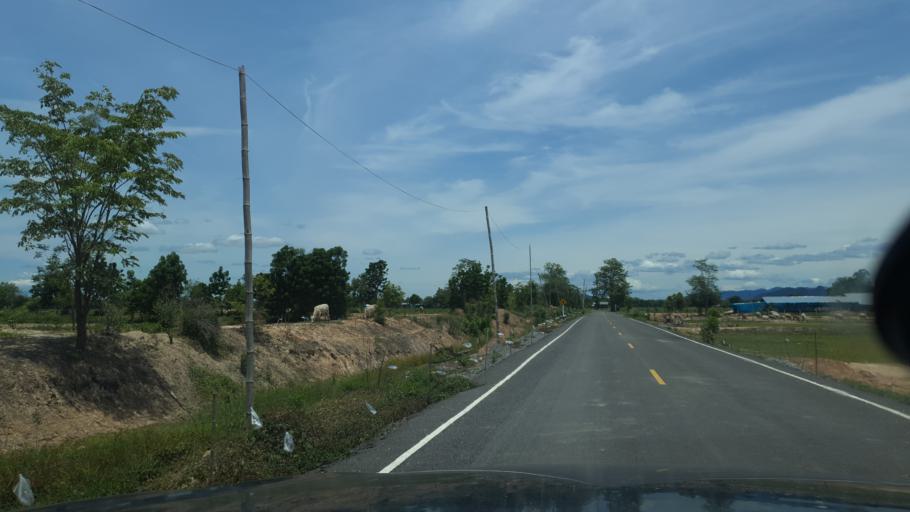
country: TH
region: Sukhothai
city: Ban Dan Lan Hoi
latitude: 17.1507
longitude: 99.6419
